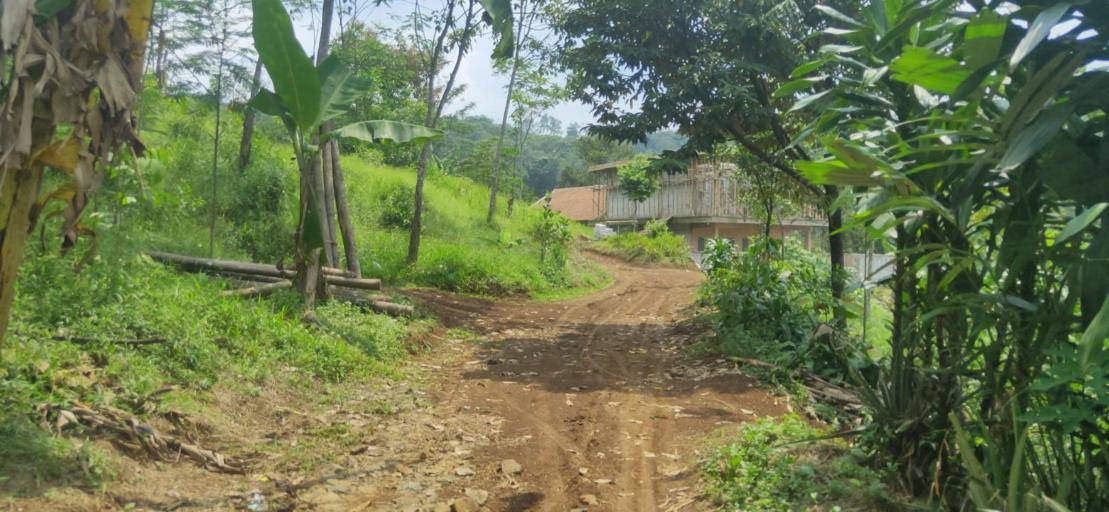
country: ID
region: West Java
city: Ciampea
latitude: -6.5331
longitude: 106.6445
